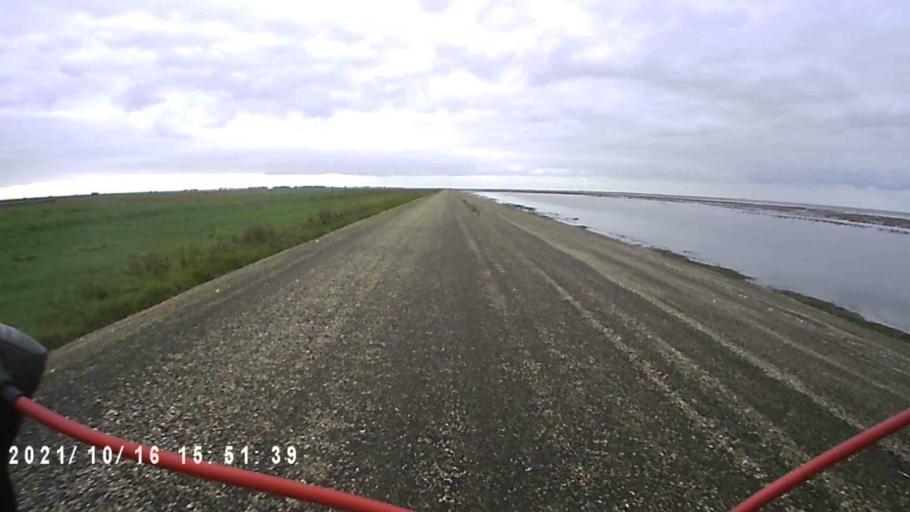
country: NL
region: Friesland
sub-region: Gemeente Dongeradeel
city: Anjum
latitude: 53.4047
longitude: 6.1312
